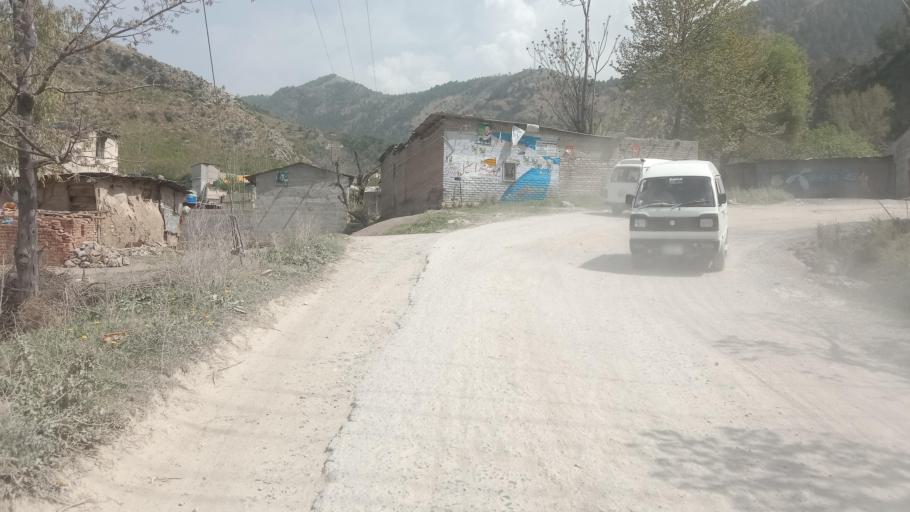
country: PK
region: Khyber Pakhtunkhwa
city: Abbottabad
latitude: 34.1621
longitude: 73.2751
